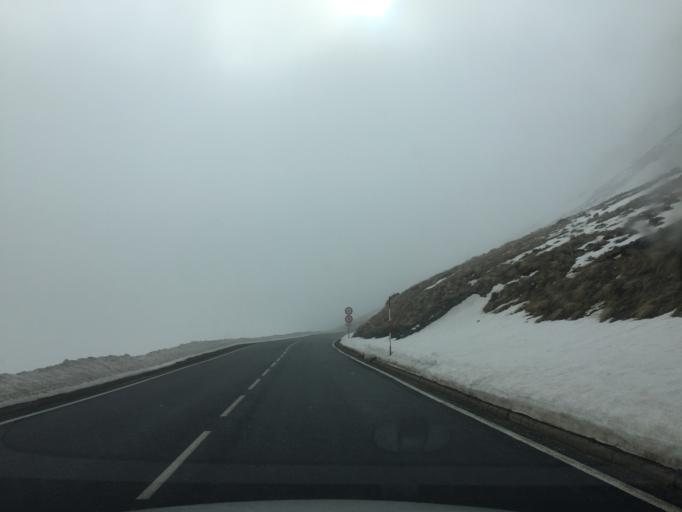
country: ES
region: Aragon
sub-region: Provincia de Huesca
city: Bielsa
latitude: 42.7532
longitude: 0.1916
